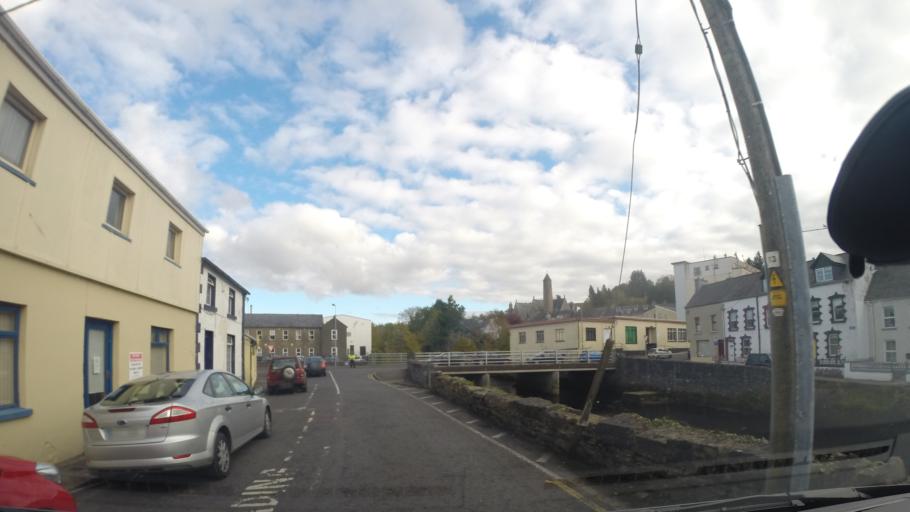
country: IE
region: Ulster
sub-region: County Donegal
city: Donegal
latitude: 54.6551
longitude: -8.1086
